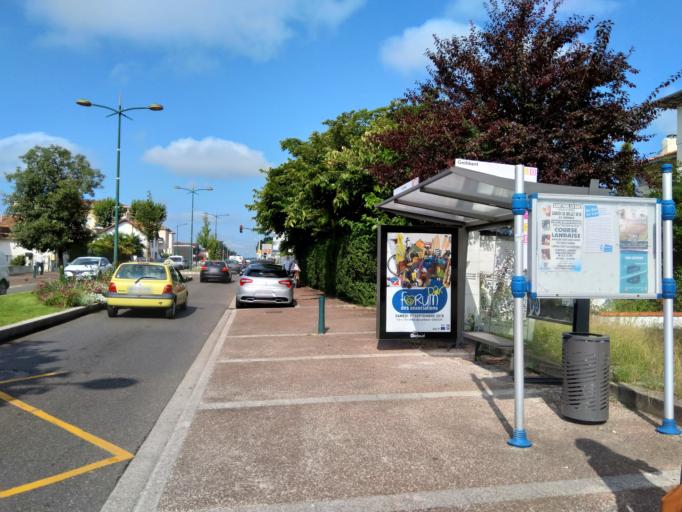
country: FR
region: Aquitaine
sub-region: Departement des Landes
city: Saint-Paul-les-Dax
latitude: 43.7243
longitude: -1.0557
